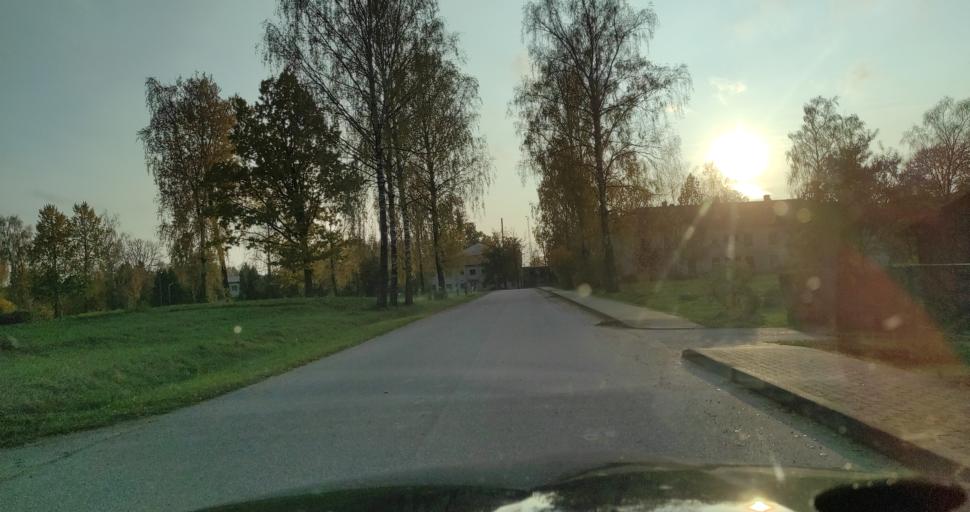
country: LV
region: Vainode
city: Vainode
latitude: 56.4188
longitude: 21.8466
